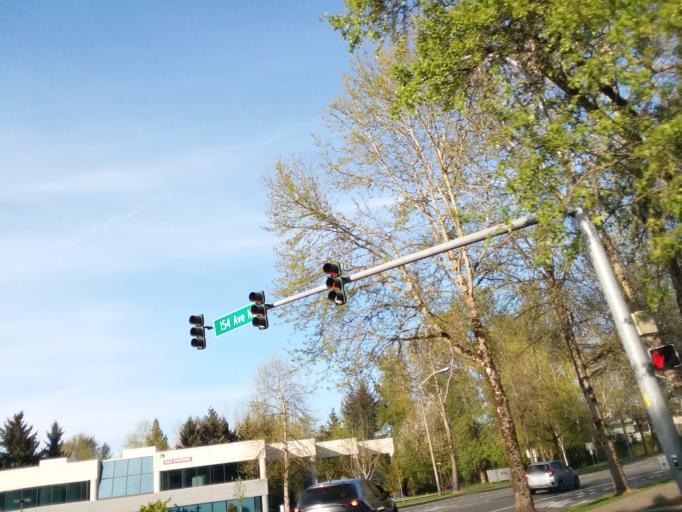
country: US
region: Washington
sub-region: King County
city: Redmond
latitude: 47.6785
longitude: -122.1347
